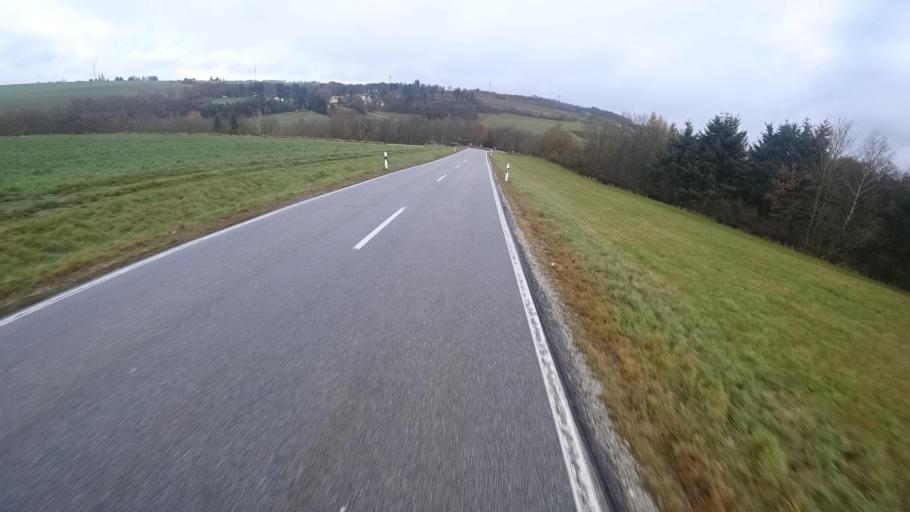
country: DE
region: Rheinland-Pfalz
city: Leiningen
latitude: 50.1358
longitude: 7.5663
